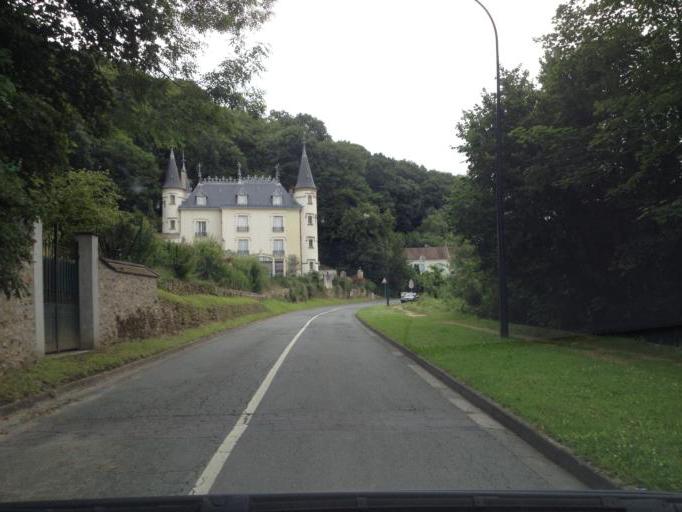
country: FR
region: Ile-de-France
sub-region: Departement de l'Essonne
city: Villiers-le-Bacle
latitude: 48.7214
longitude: 2.1222
